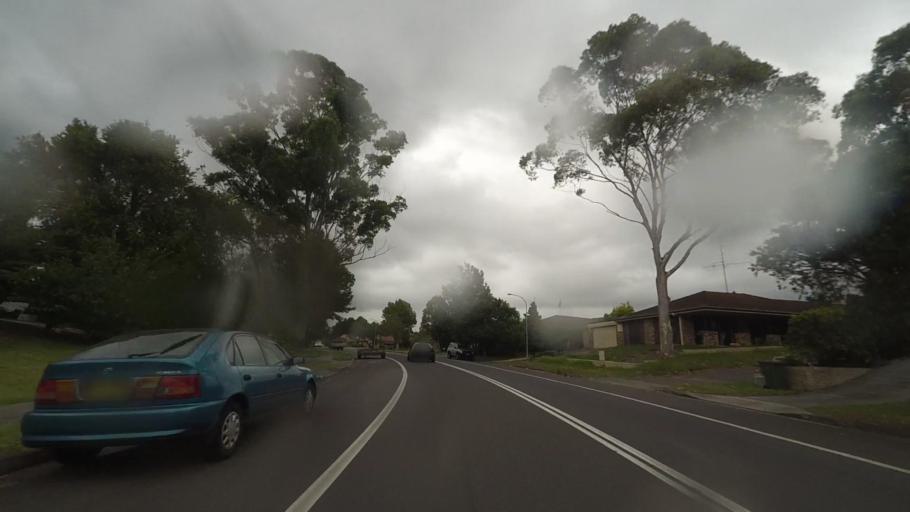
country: AU
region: New South Wales
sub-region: Wollongong
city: Cordeaux Heights
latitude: -34.4425
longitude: 150.8455
